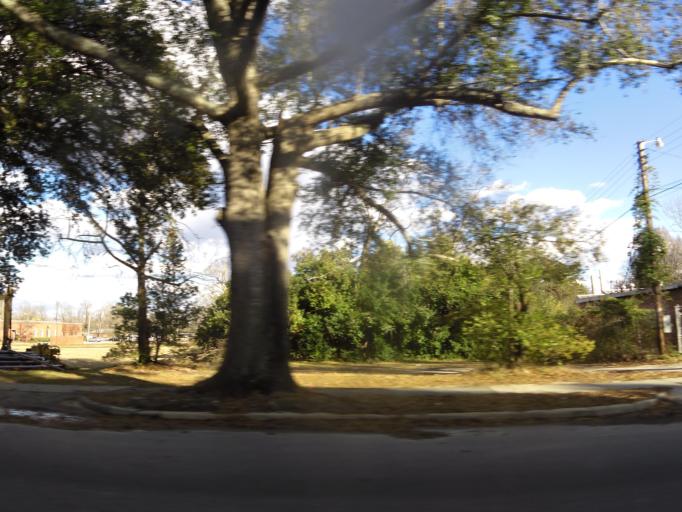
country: US
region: South Carolina
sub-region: Clarendon County
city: Manning
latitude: 33.6934
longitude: -80.2092
